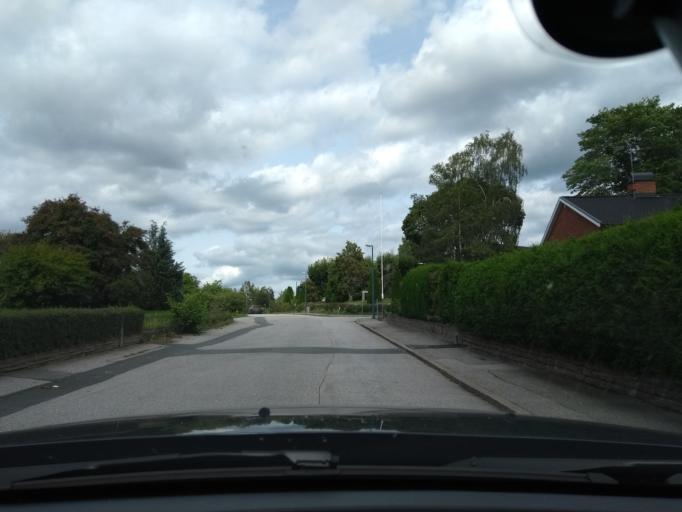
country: SE
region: Kalmar
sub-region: Vimmerby Kommun
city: Vimmerby
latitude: 57.6743
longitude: 15.8620
